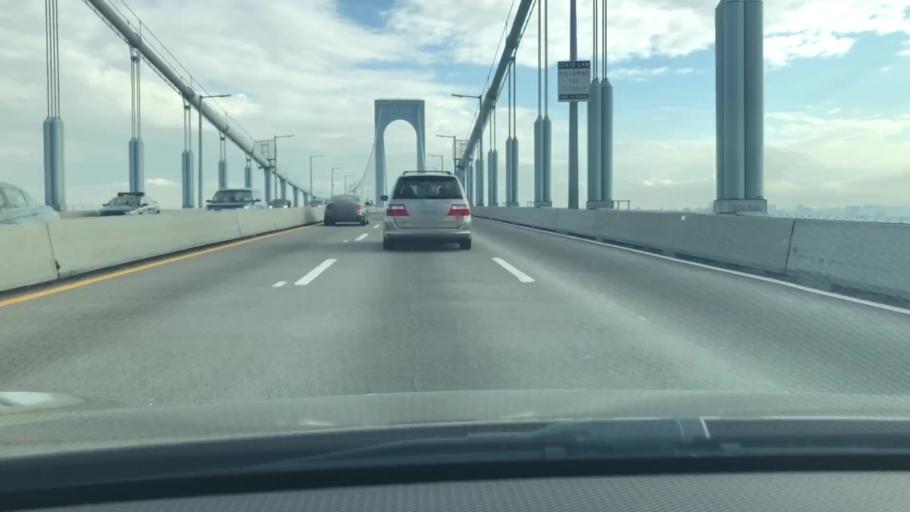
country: US
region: New York
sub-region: Bronx
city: The Bronx
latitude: 40.8034
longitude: -73.8307
